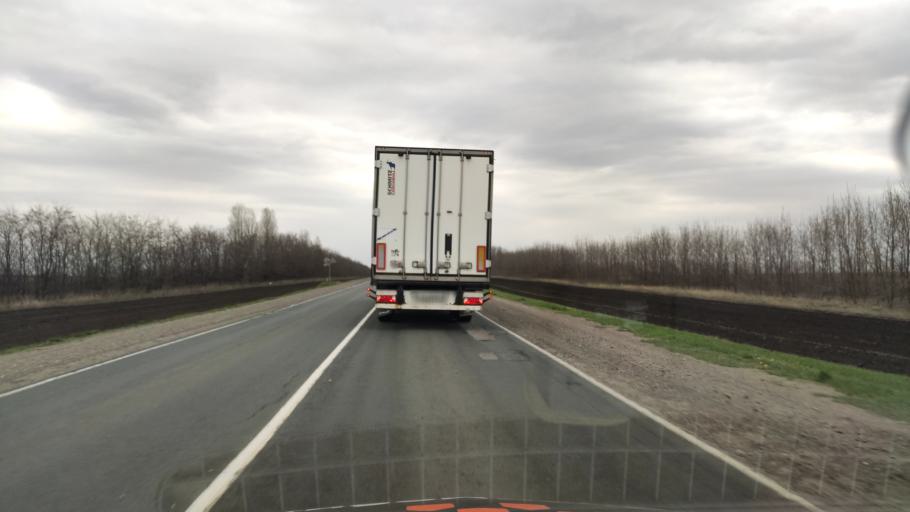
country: RU
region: Voronezj
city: Nizhnedevitsk
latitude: 51.5722
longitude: 38.3314
